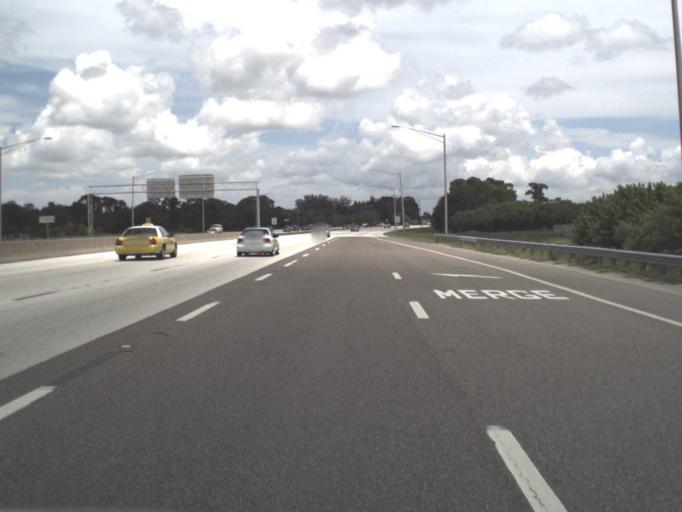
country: US
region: Florida
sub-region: Pinellas County
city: South Highpoint
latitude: 27.9140
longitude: -82.7002
